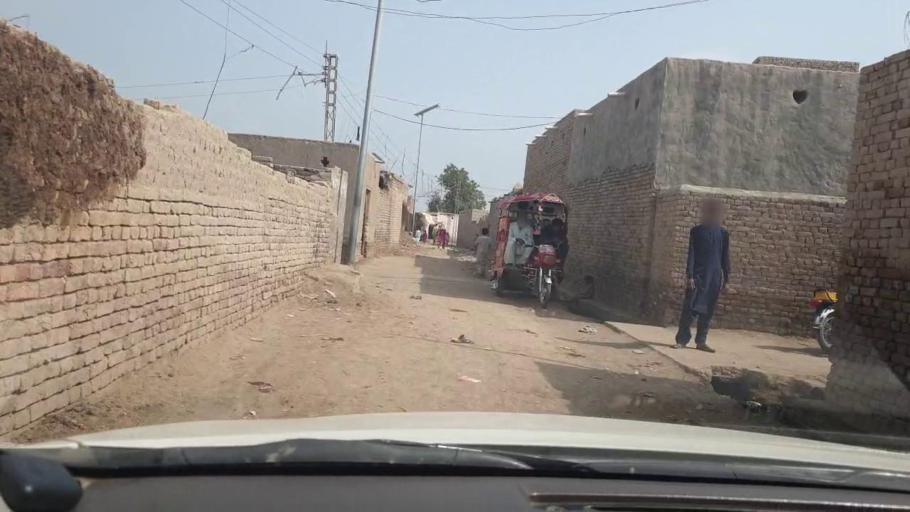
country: PK
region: Sindh
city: Shikarpur
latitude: 28.0064
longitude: 68.5930
